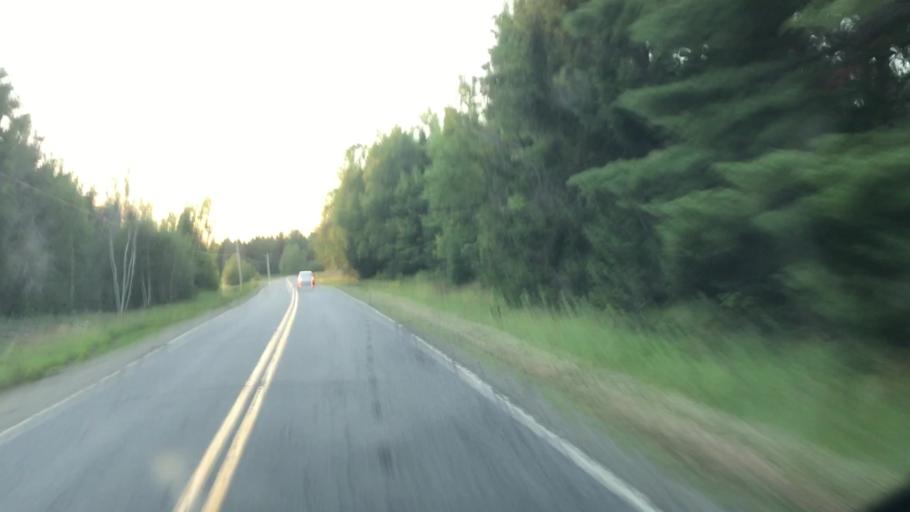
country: US
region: Maine
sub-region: Penobscot County
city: Medway
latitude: 45.6047
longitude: -68.2535
